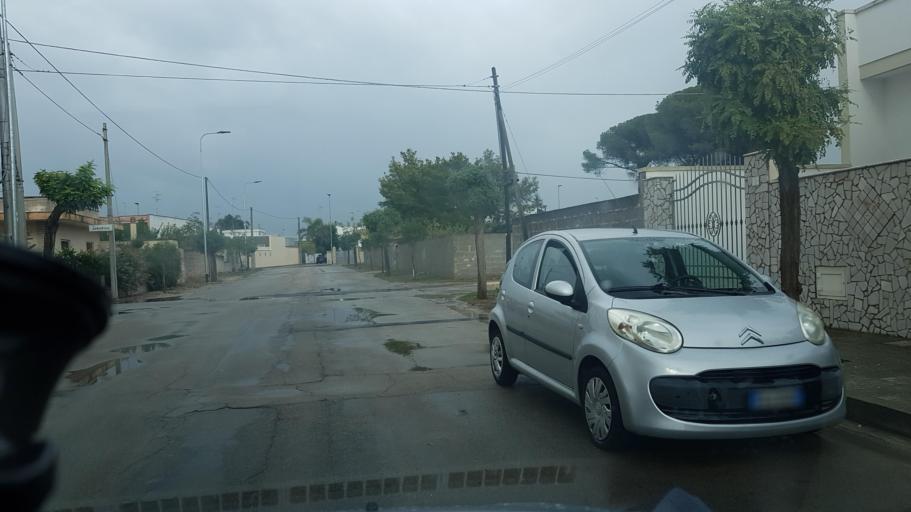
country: IT
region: Apulia
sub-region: Provincia di Lecce
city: Carmiano
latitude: 40.3399
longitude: 18.0476
